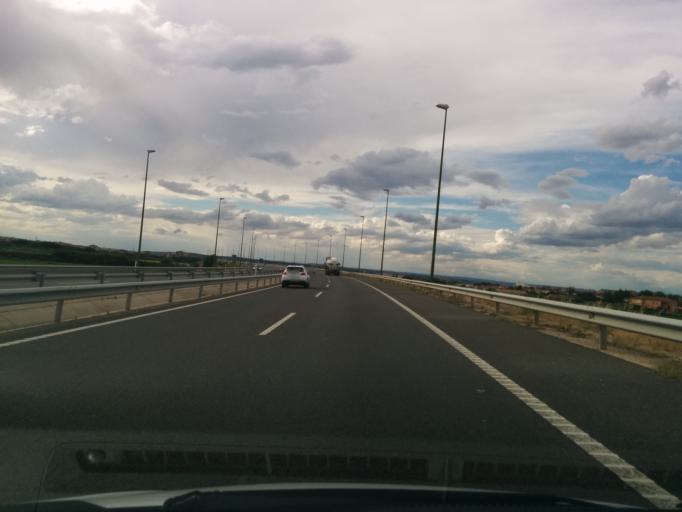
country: ES
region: Aragon
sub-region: Provincia de Zaragoza
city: Zaragoza
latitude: 41.6458
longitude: -0.8325
